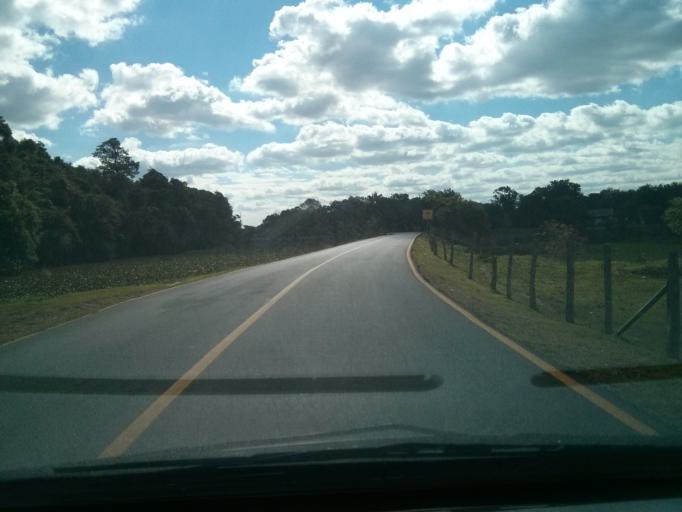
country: BR
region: Parana
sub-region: Sao Jose Dos Pinhais
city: Sao Jose dos Pinhais
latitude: -25.5563
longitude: -49.2264
